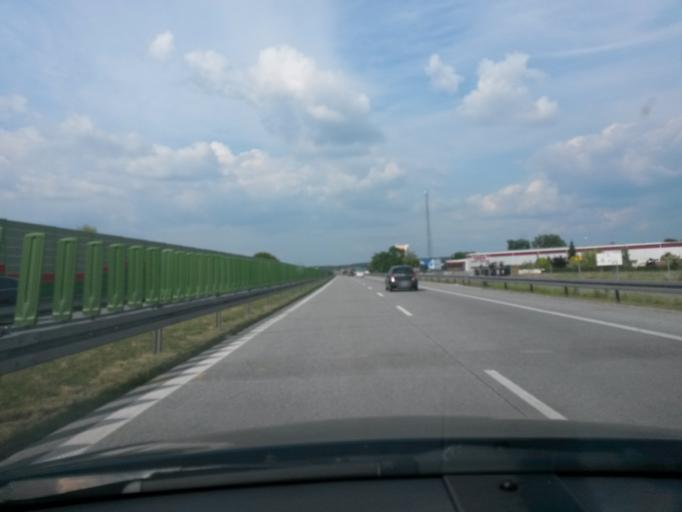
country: PL
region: Lodz Voivodeship
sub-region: Powiat rawski
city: Rawa Mazowiecka
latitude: 51.7564
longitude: 20.2578
